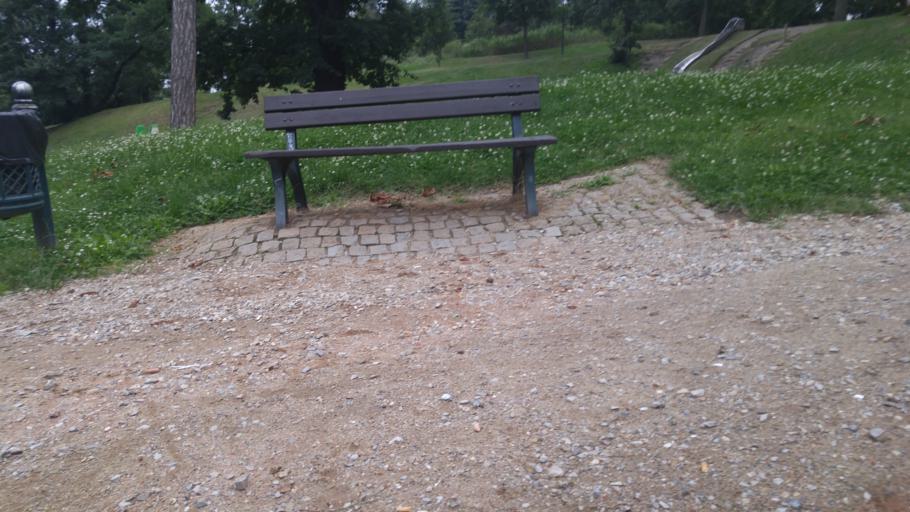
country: CZ
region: Praha
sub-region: Praha 1
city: Mala Strana
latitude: 50.0748
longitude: 14.3995
